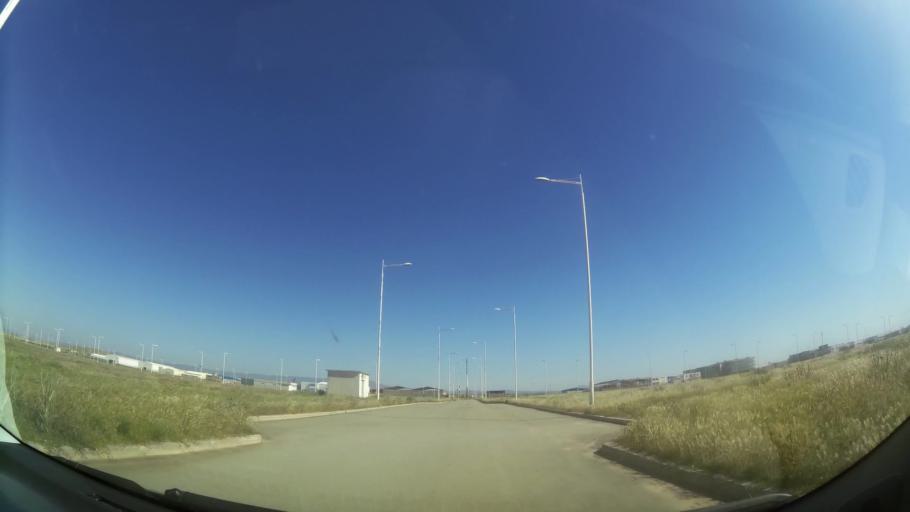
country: MA
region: Oriental
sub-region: Oujda-Angad
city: Oujda
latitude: 34.7741
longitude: -1.9357
